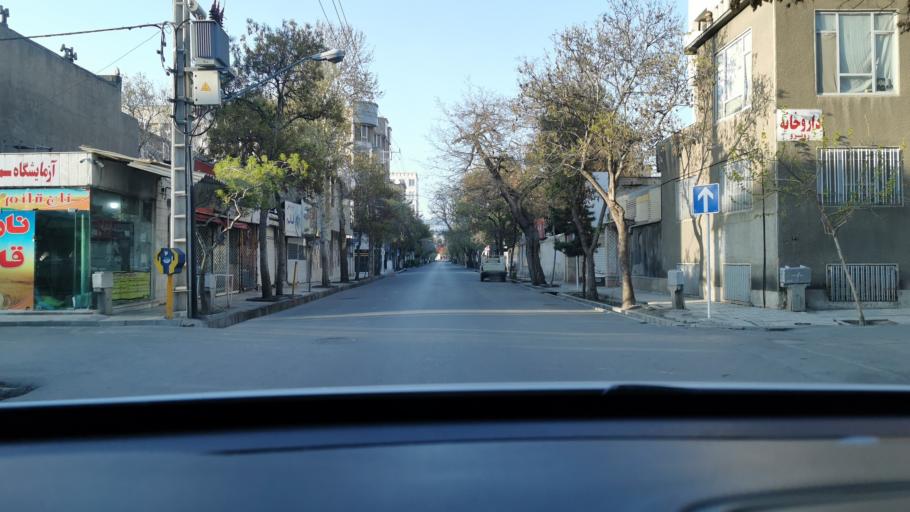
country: IR
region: Razavi Khorasan
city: Mashhad
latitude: 36.2989
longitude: 59.5804
